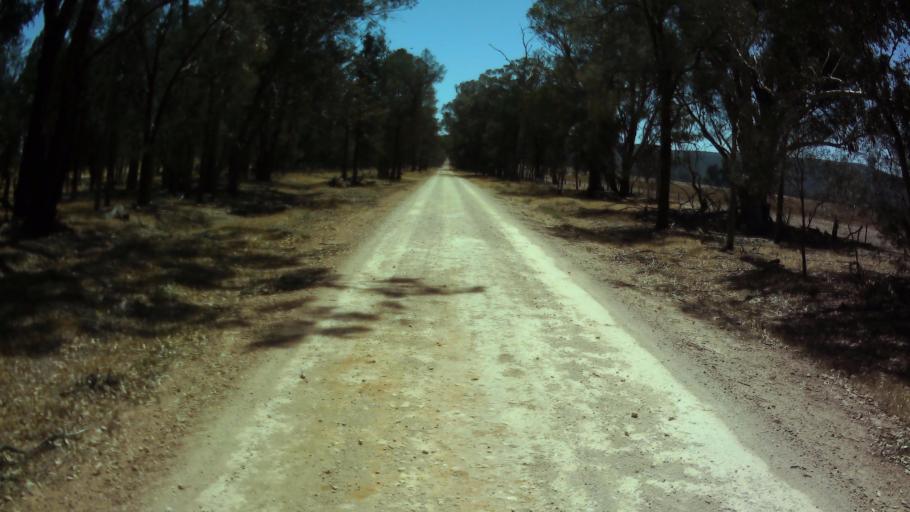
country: AU
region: New South Wales
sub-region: Weddin
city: Grenfell
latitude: -34.0020
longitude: 147.9566
